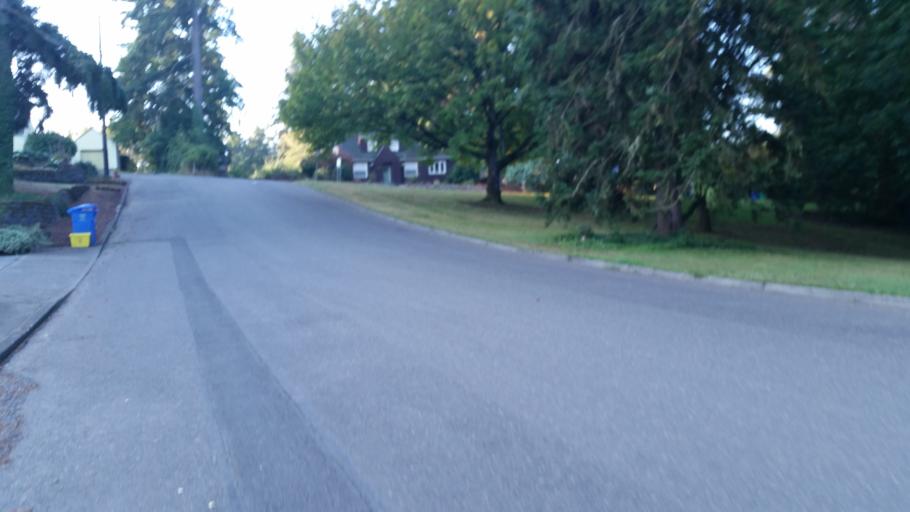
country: US
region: Oregon
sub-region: Washington County
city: Garden Home-Whitford
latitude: 45.4731
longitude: -122.7155
